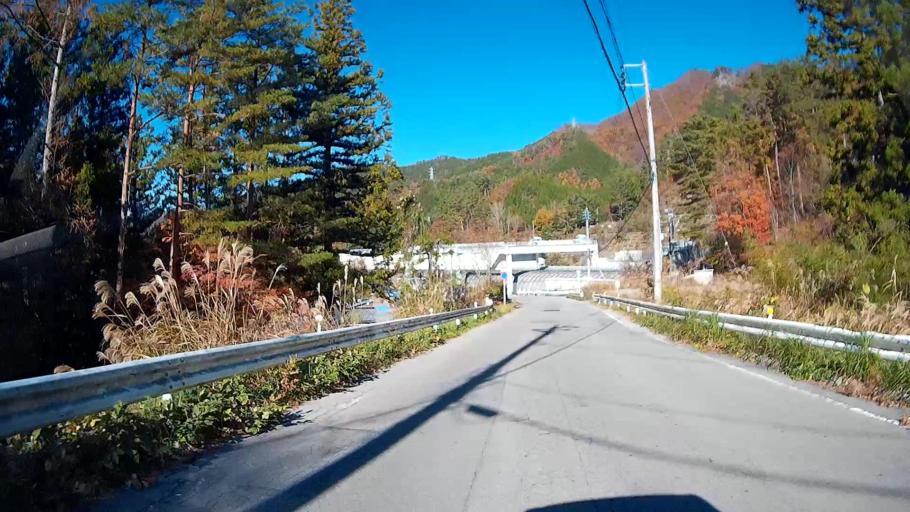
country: JP
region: Yamanashi
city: Otsuki
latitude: 35.5614
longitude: 139.0074
